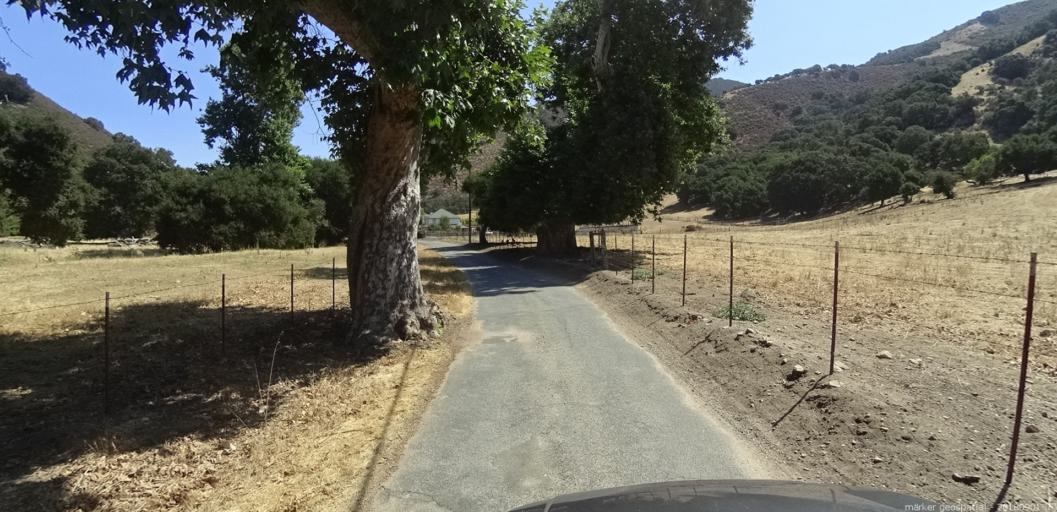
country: US
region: California
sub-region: Monterey County
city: Gonzales
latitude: 36.6038
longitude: -121.4024
